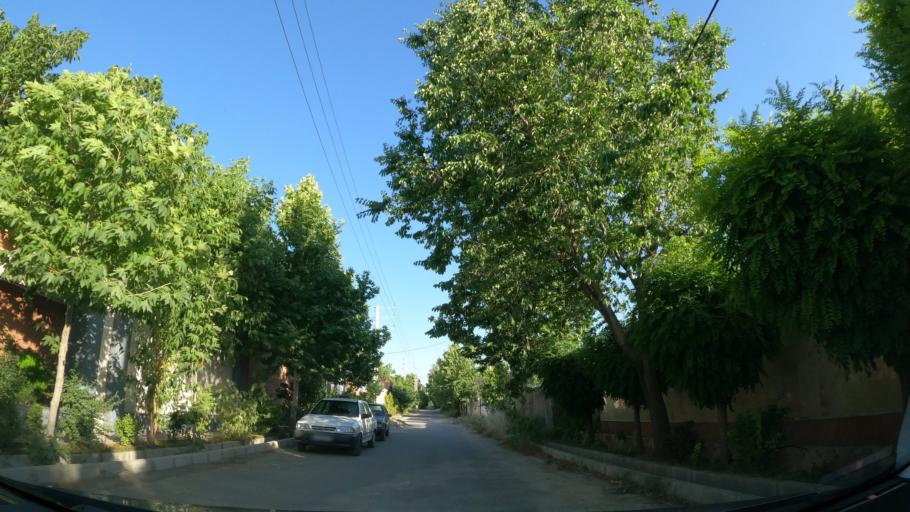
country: IR
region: Alborz
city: Hashtgerd
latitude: 35.9113
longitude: 50.7211
